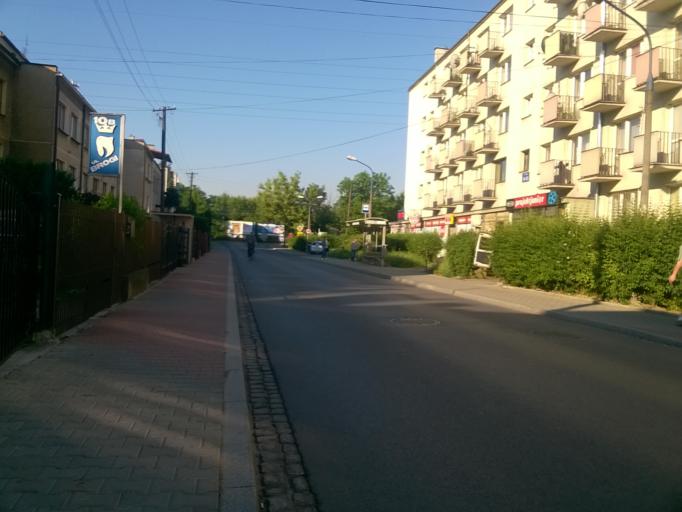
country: PL
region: Lesser Poland Voivodeship
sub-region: Krakow
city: Krakow
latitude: 50.0801
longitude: 19.9613
